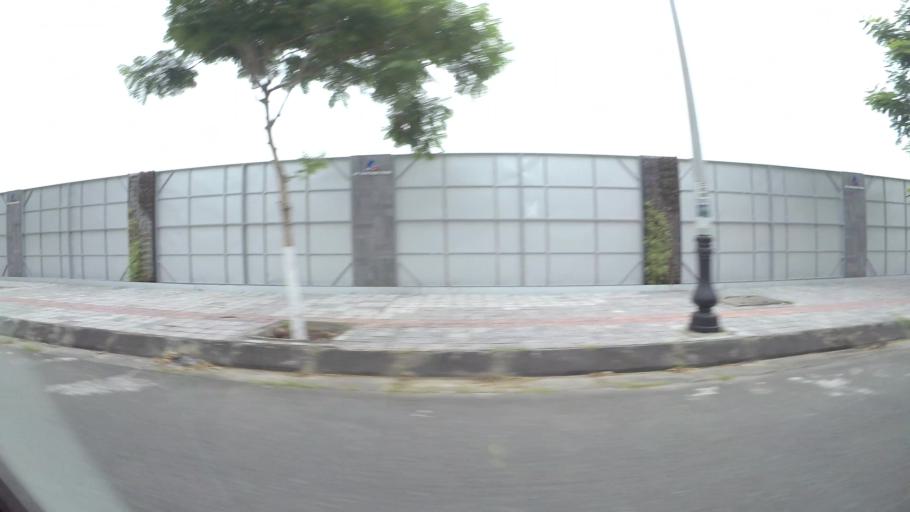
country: VN
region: Da Nang
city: Son Tra
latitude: 16.0339
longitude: 108.2303
